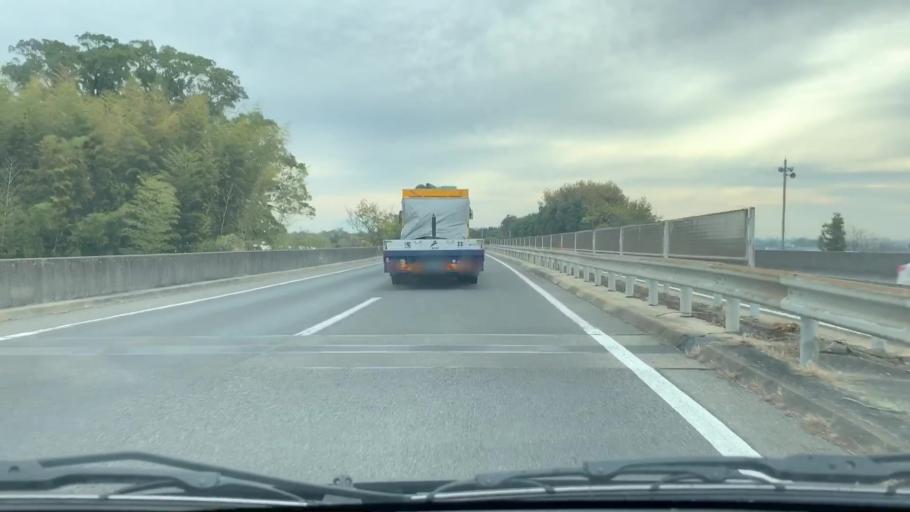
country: JP
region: Saga Prefecture
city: Saga-shi
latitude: 33.3073
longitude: 130.2299
